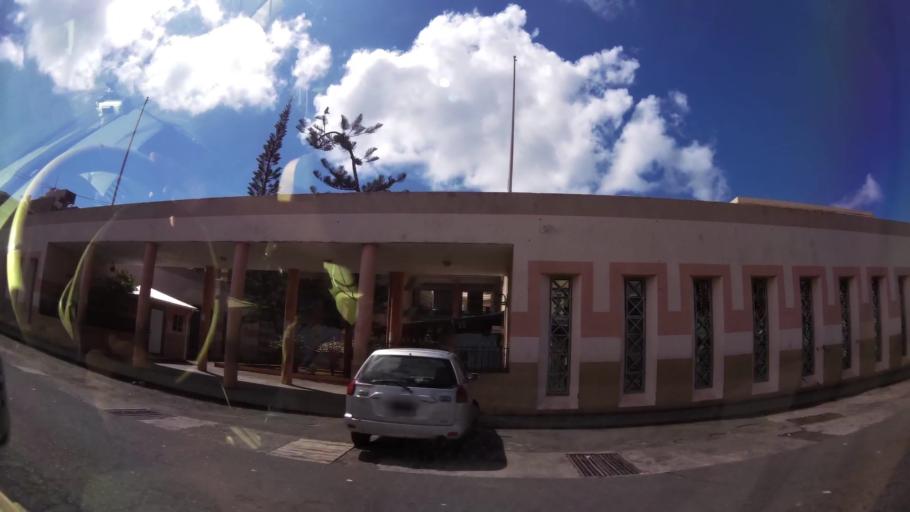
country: VC
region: Saint George
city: Kingstown
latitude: 13.1553
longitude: -61.2254
